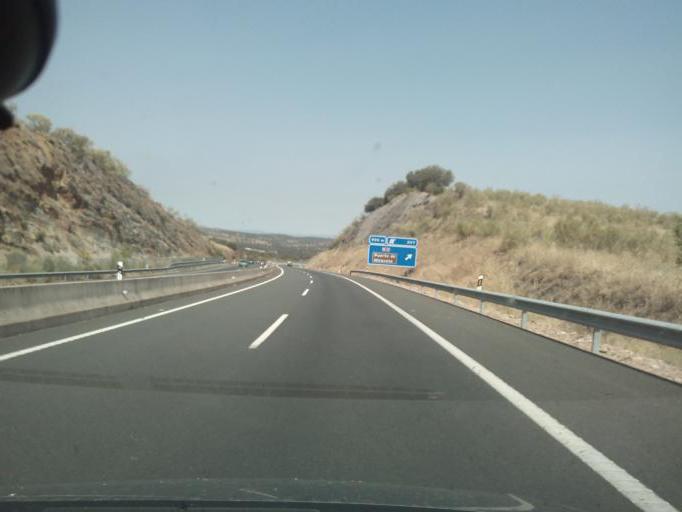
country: ES
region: Extremadura
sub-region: Provincia de Caceres
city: Romangordo
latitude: 39.7548
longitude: -5.7265
